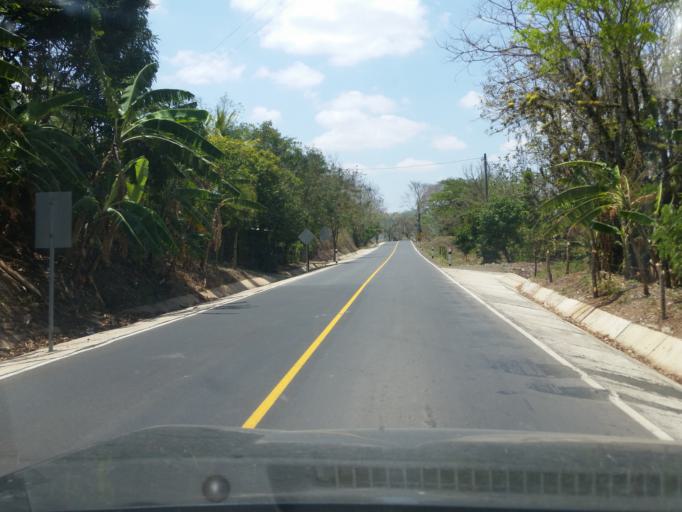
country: NI
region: Boaco
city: Boaco
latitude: 12.5694
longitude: -85.5451
